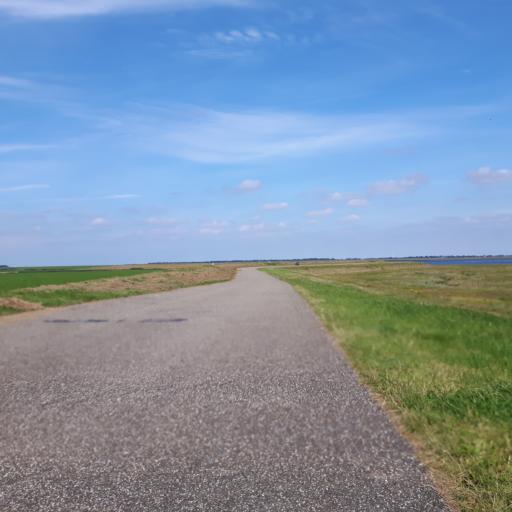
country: NL
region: Zeeland
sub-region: Schouwen-Duiveland
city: Bruinisse
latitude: 51.6433
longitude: 4.1595
